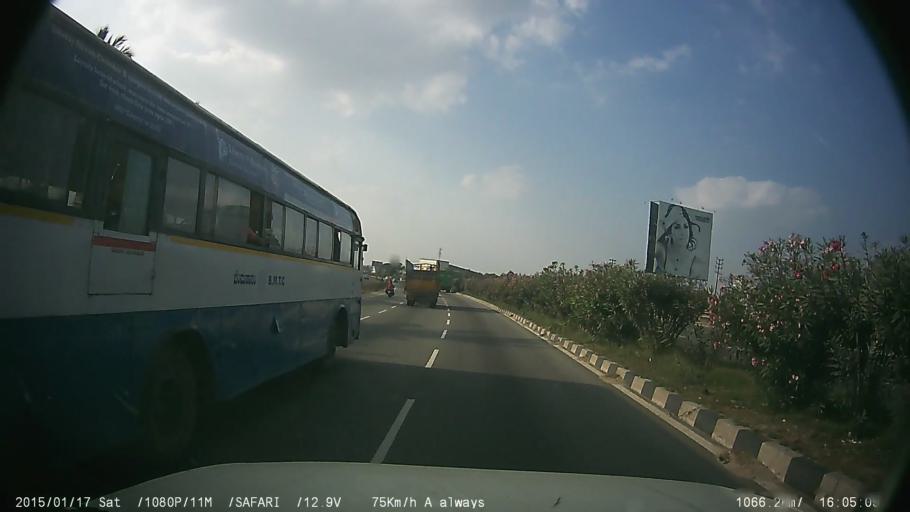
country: IN
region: Karnataka
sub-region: Bangalore Urban
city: Anekal
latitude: 12.7978
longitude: 77.7173
